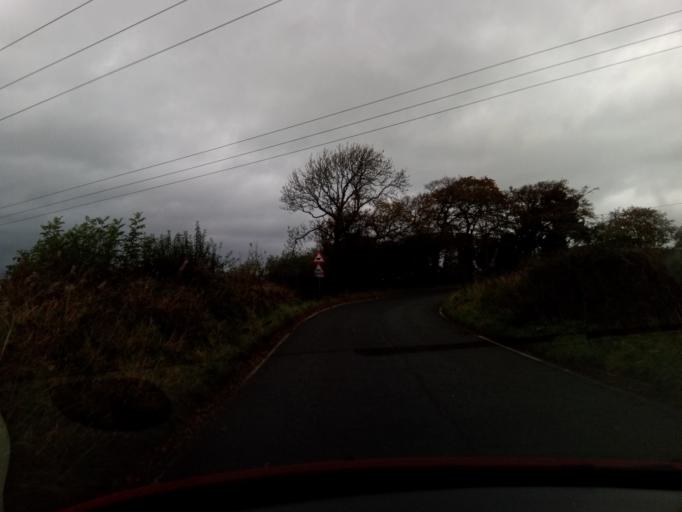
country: GB
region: Scotland
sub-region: West Lothian
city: Bathgate
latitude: 55.9160
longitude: -3.6380
